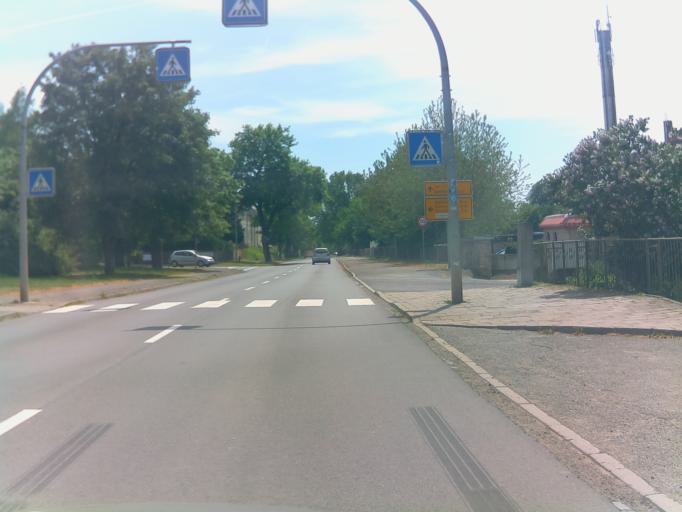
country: DE
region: Saxony-Anhalt
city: Hedersleben
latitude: 51.8547
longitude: 11.2530
